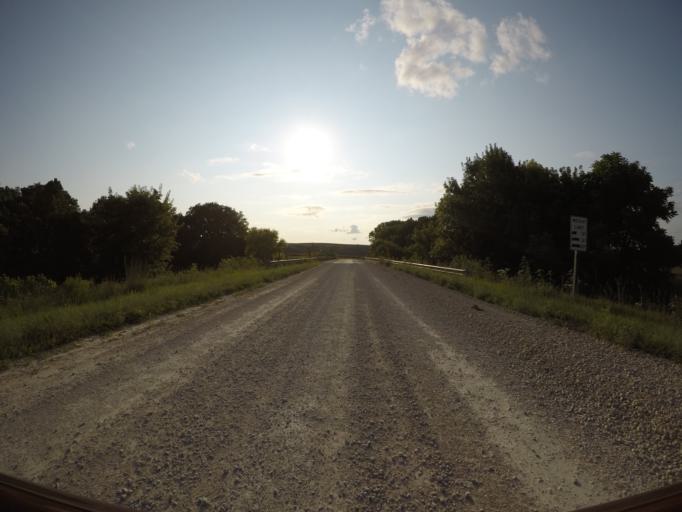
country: US
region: Kansas
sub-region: Wabaunsee County
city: Alma
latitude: 38.9516
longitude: -96.2446
